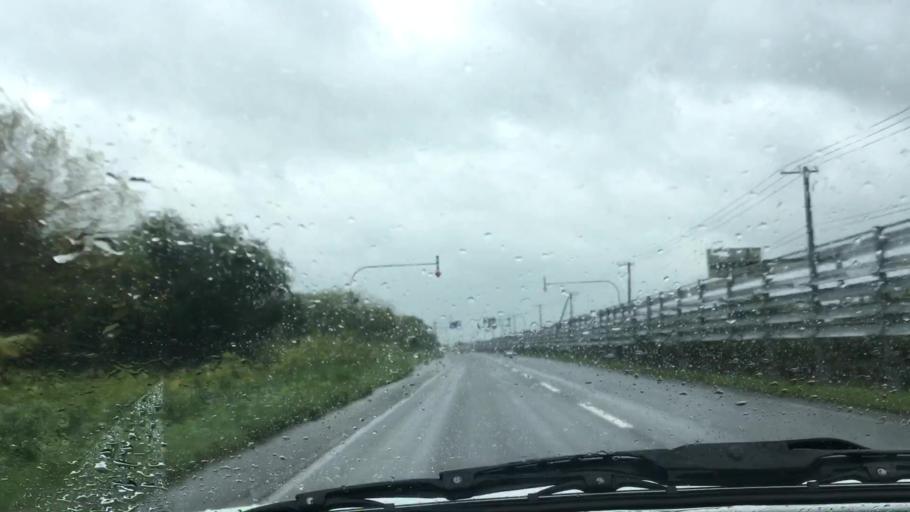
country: JP
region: Hokkaido
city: Nanae
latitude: 42.3067
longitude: 140.2725
